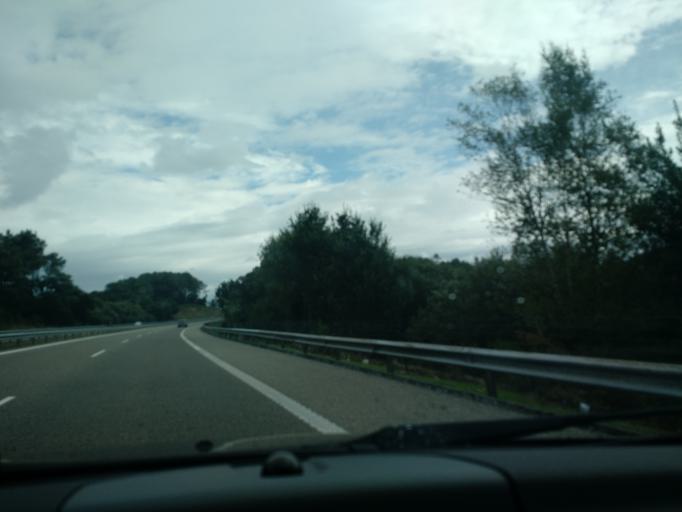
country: ES
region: Galicia
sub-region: Provincia da Coruna
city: Abegondo
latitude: 43.2260
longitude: -8.2728
